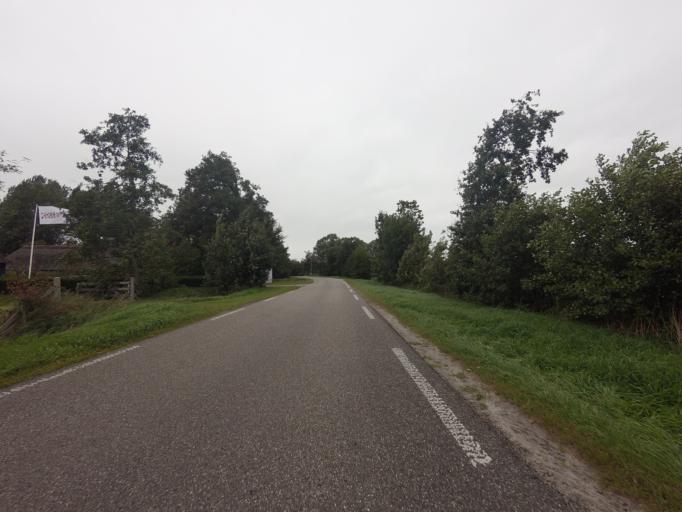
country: NL
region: Friesland
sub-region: Gemeente Opsterland
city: Tijnje
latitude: 53.0247
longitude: 6.0028
